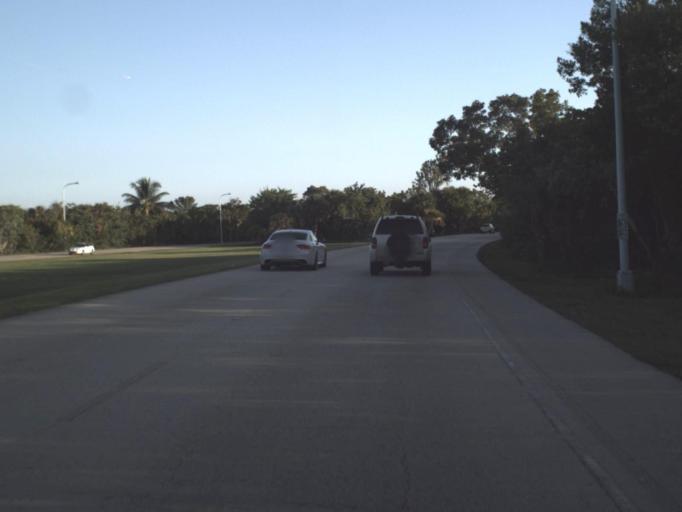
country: US
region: Florida
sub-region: Miami-Dade County
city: Key Biscayne
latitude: 25.7238
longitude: -80.1517
